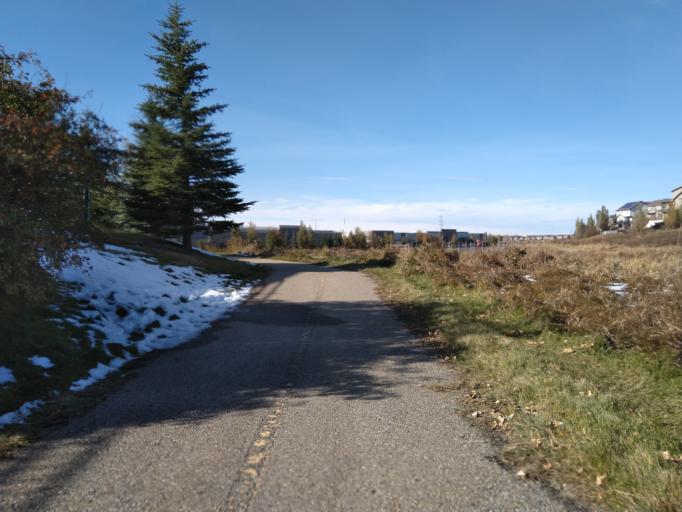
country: CA
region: Alberta
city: Calgary
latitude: 51.1624
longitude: -114.1230
